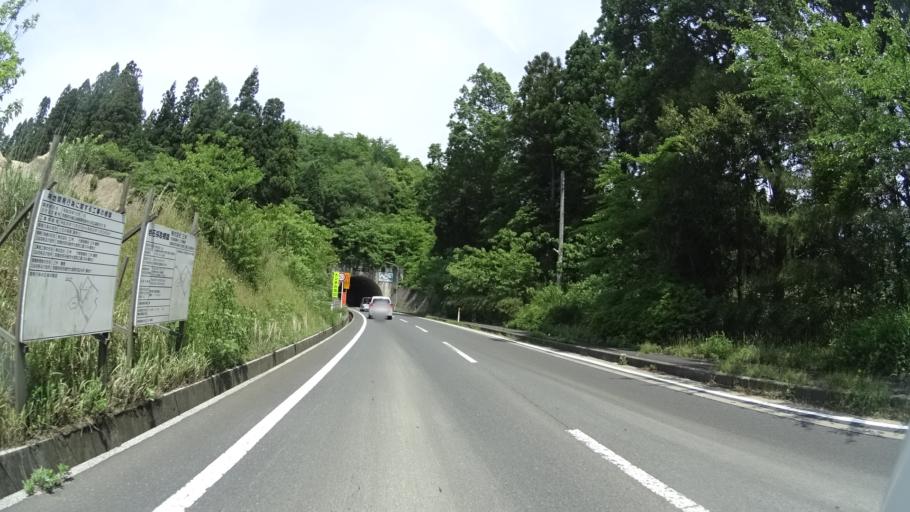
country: JP
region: Kyoto
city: Miyazu
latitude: 35.5814
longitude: 135.1177
